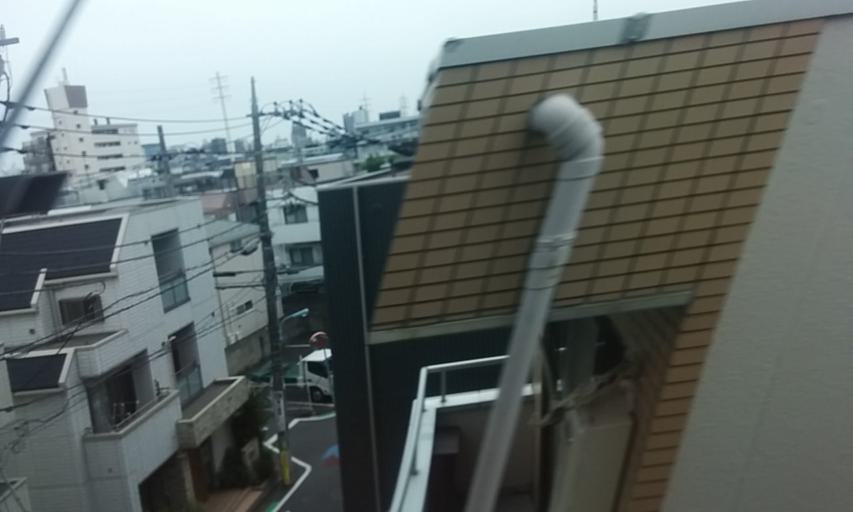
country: JP
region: Tokyo
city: Tokyo
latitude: 35.7051
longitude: 139.6447
